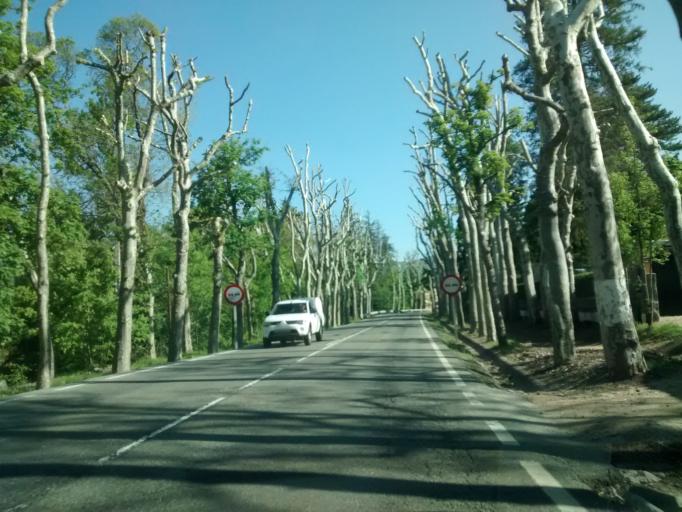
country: ES
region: Castille and Leon
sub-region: Provincia de Segovia
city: San Ildefonso
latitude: 40.8970
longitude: -4.0123
